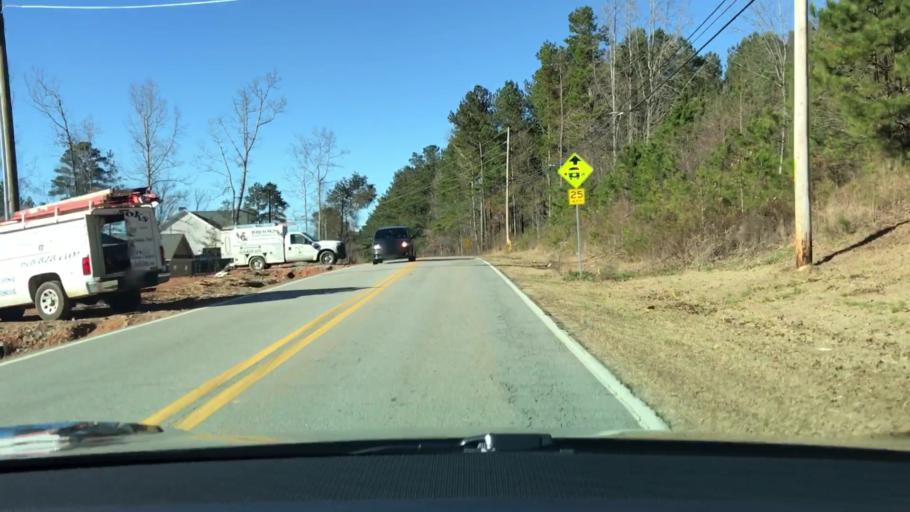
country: US
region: Georgia
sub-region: Barrow County
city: Auburn
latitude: 34.0460
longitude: -83.8448
